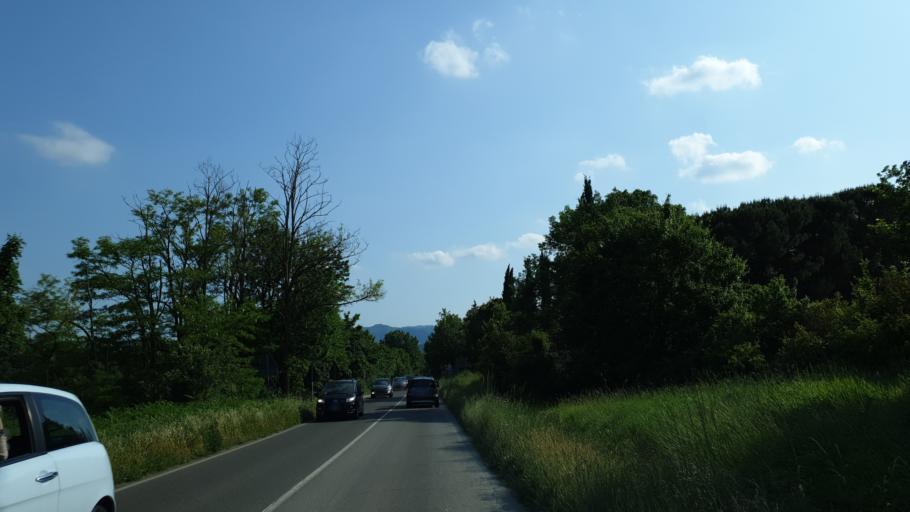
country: IT
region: Tuscany
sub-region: Province of Arezzo
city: Soci
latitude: 43.7344
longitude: 11.7917
